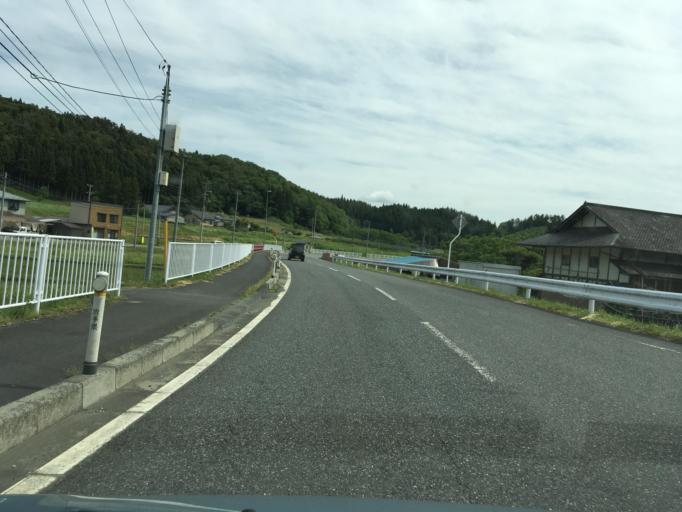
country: JP
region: Iwate
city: Mizusawa
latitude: 39.0809
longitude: 141.3535
